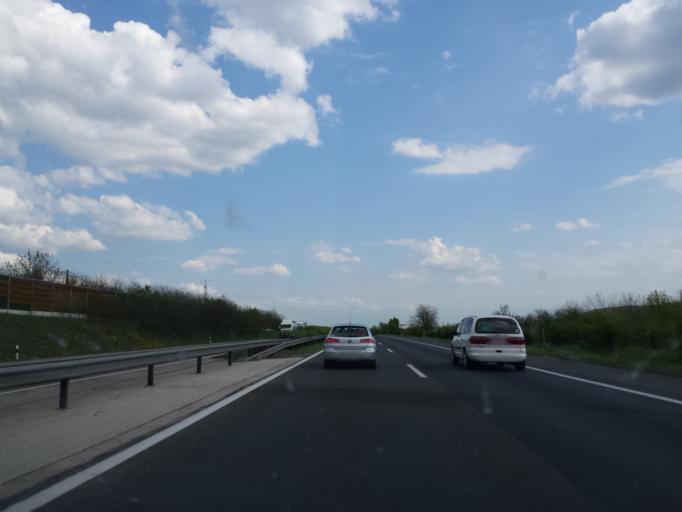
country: HU
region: Pest
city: Biatorbagy
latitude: 47.4802
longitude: 18.8430
